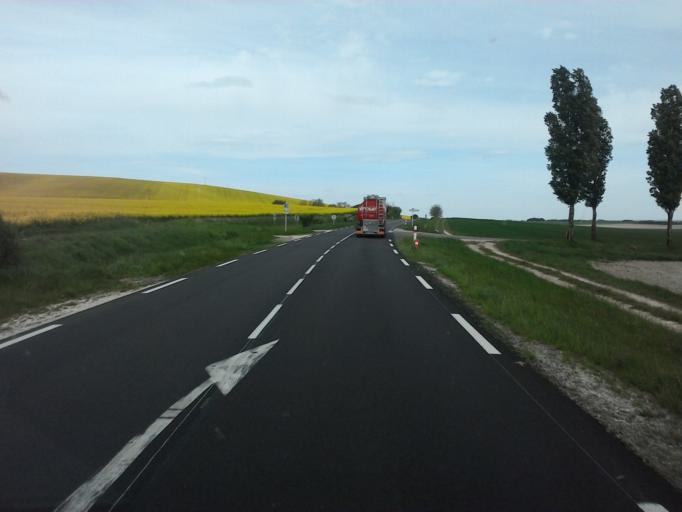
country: FR
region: Champagne-Ardenne
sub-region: Departement de l'Aube
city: Bouilly
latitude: 48.1334
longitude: 3.9839
